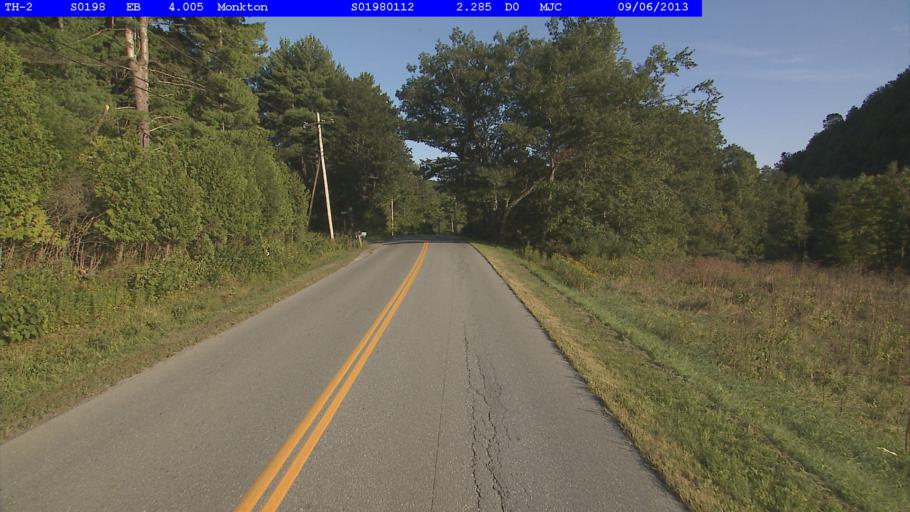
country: US
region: Vermont
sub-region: Chittenden County
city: Hinesburg
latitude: 44.2421
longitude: -73.1570
